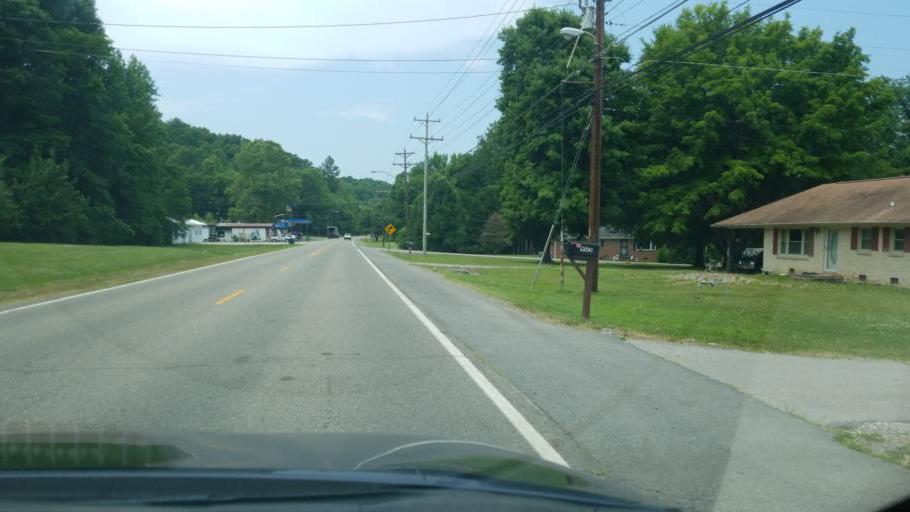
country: US
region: Tennessee
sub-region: Humphreys County
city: Waverly
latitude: 36.0799
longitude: -87.8283
